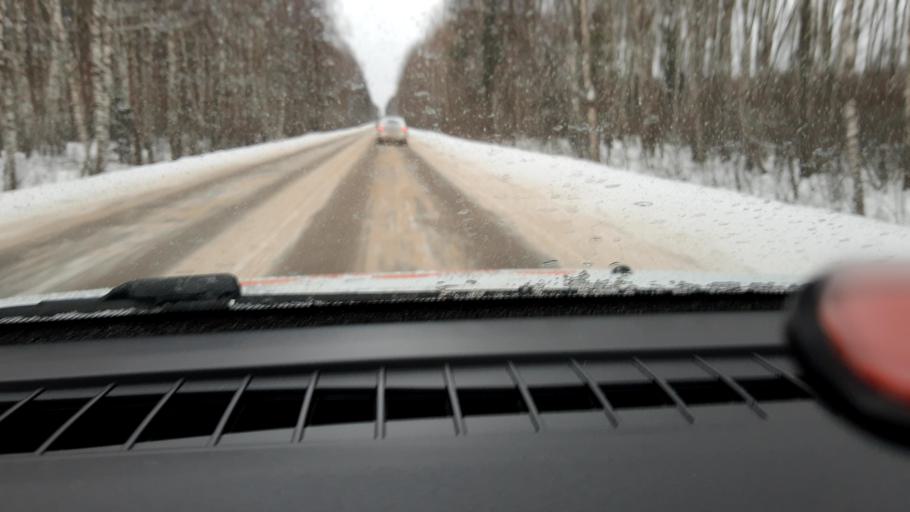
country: RU
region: Nizjnij Novgorod
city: Kstovo
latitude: 56.2875
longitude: 44.2988
